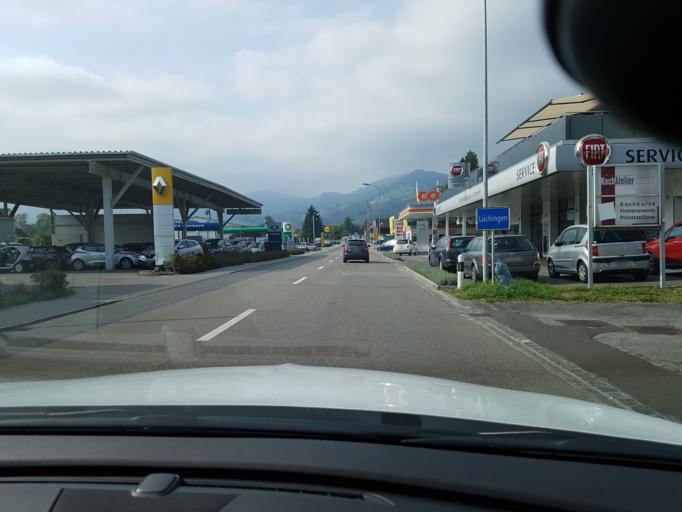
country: CH
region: Saint Gallen
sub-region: Wahlkreis Rheintal
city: Altstatten
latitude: 47.3895
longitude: 9.5628
